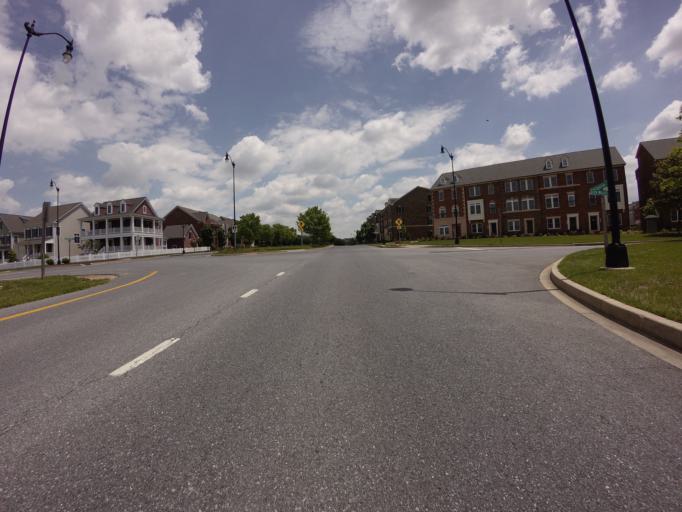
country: US
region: Maryland
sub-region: Frederick County
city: Urbana
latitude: 39.3308
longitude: -77.3600
